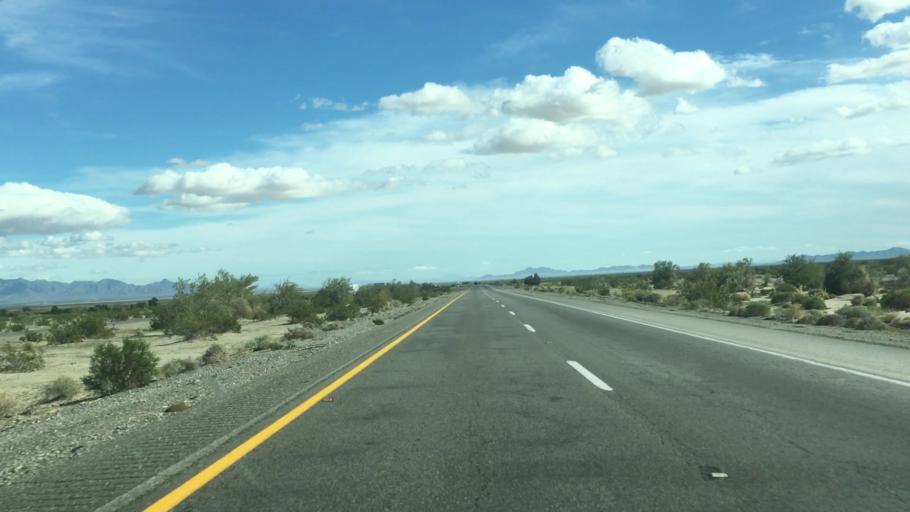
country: US
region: California
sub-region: Riverside County
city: Mesa Verde
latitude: 33.6531
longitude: -115.1449
